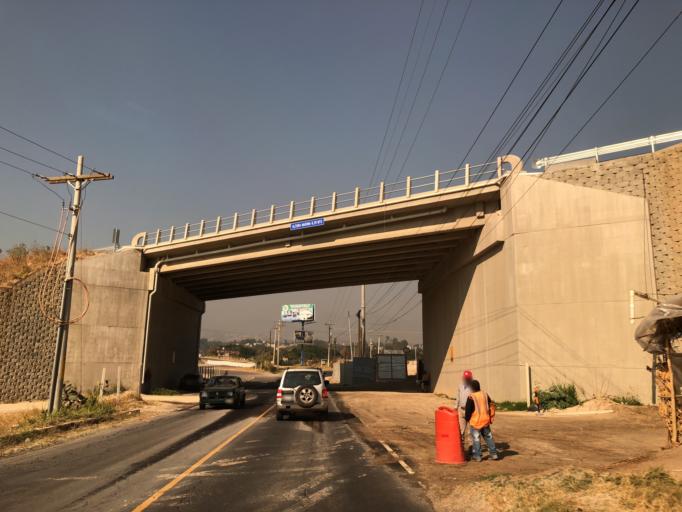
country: GT
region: Guatemala
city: Petapa
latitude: 14.5023
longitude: -90.5423
